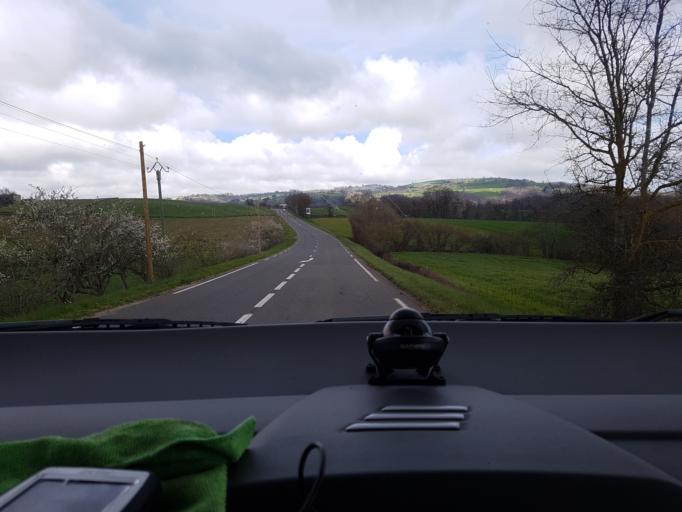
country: FR
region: Midi-Pyrenees
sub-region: Departement de l'Aveyron
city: Moyrazes
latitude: 44.3870
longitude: 2.4002
